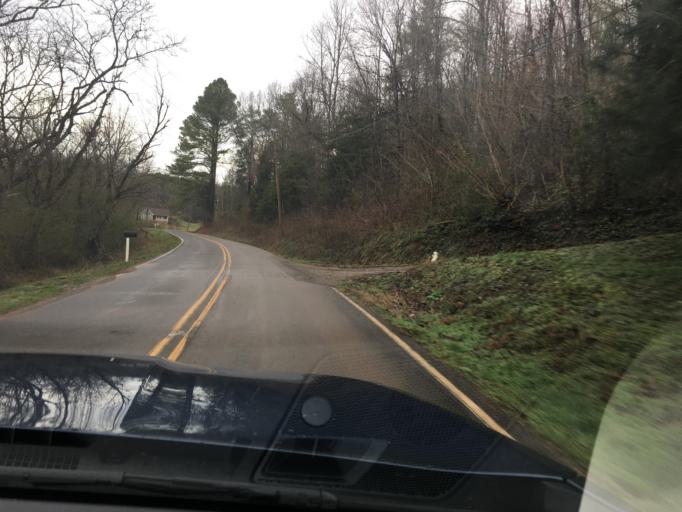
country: US
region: Tennessee
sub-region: McMinn County
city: Englewood
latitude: 35.3799
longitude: -84.4372
